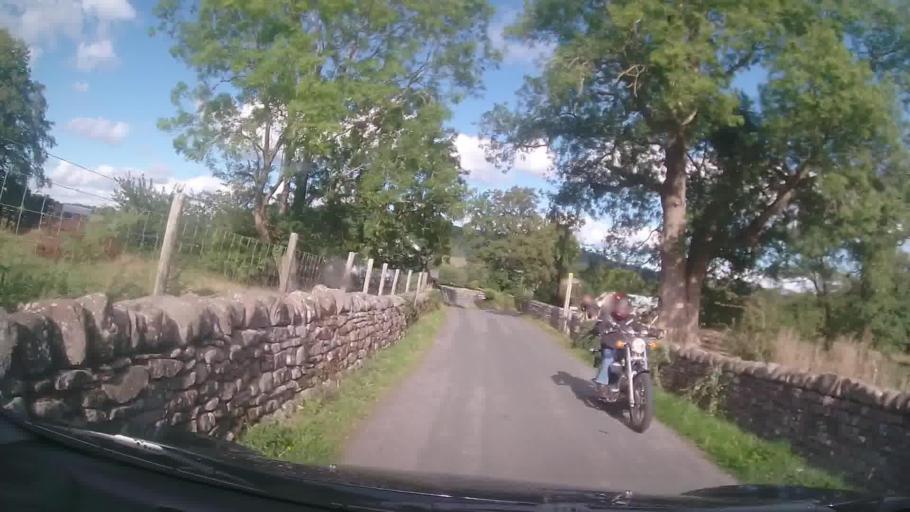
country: GB
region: Wales
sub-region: Sir Powys
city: Brecon
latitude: 51.8943
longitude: -3.2956
